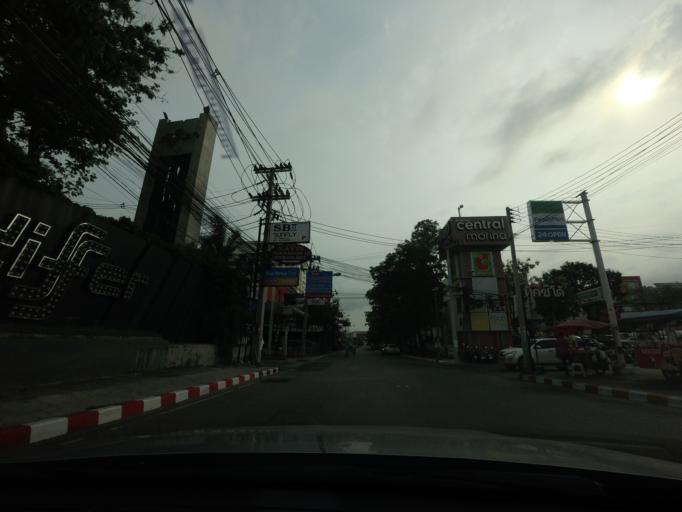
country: TH
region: Chon Buri
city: Phatthaya
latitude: 12.9465
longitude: 100.8918
